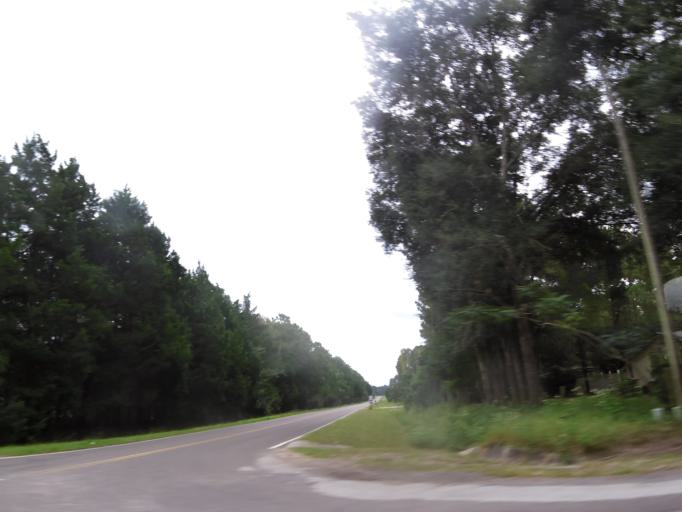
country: US
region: Florida
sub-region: Clay County
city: Middleburg
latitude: 30.0988
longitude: -81.9490
